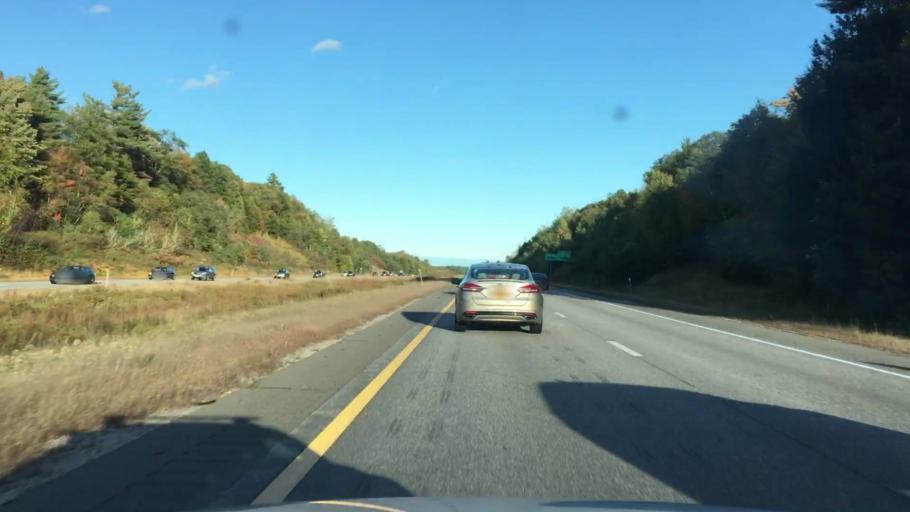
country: US
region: New Hampshire
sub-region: Rockingham County
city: Raymond
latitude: 43.0220
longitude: -71.2240
